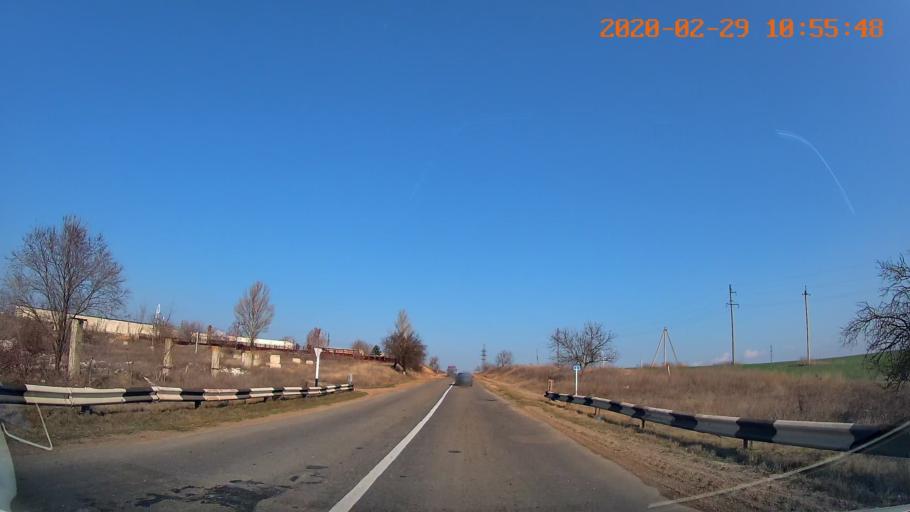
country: MD
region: Telenesti
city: Grigoriopol
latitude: 47.1380
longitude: 29.3255
